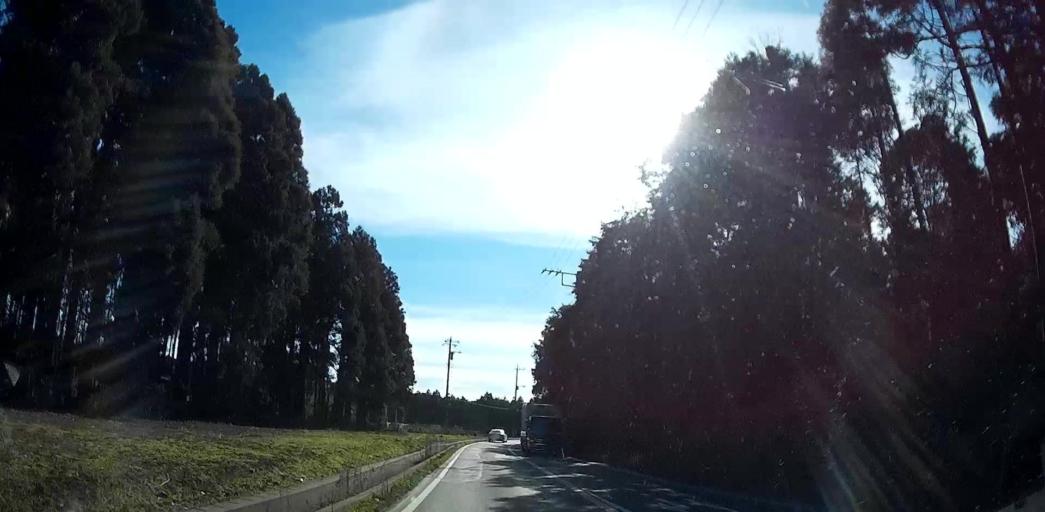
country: JP
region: Chiba
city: Yokaichiba
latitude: 35.7580
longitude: 140.4564
